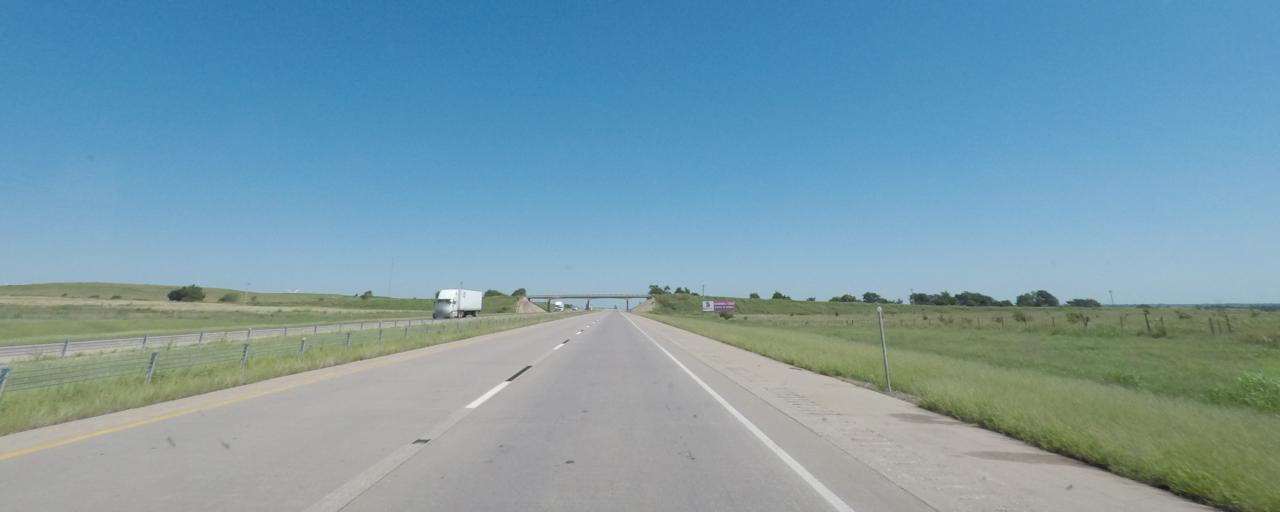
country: US
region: Oklahoma
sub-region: Kay County
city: Tonkawa
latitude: 36.5763
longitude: -97.3456
